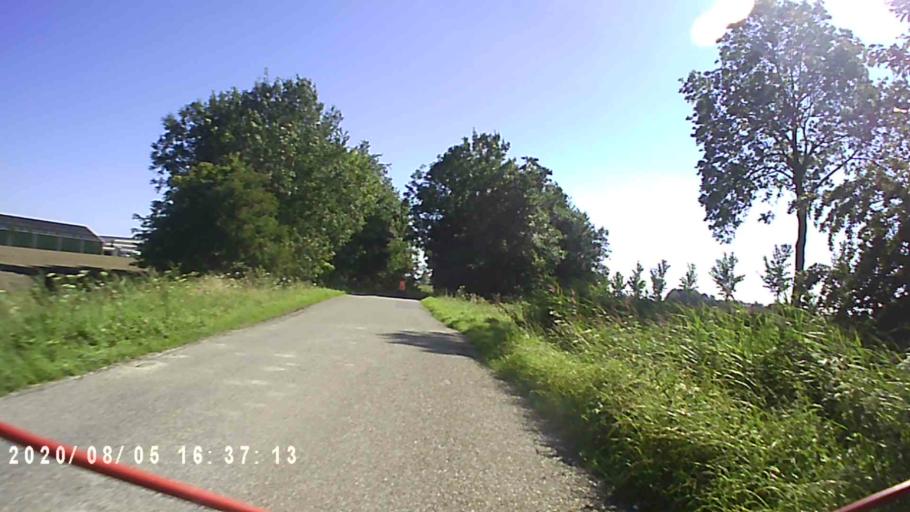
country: NL
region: Groningen
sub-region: Gemeente Winsum
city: Winsum
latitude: 53.3558
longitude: 6.5077
